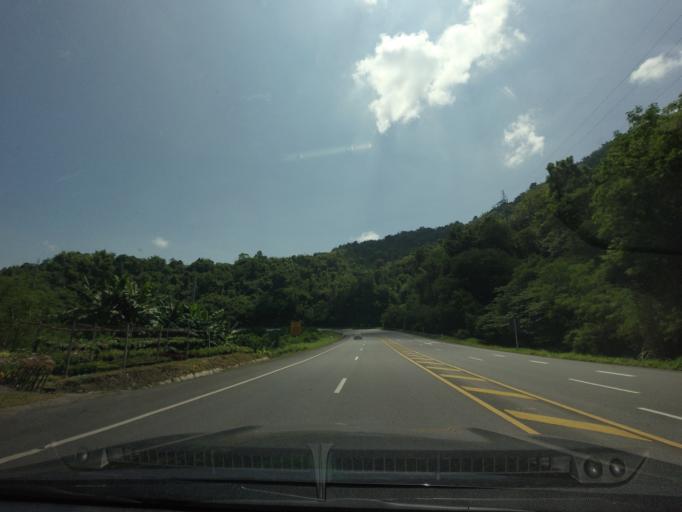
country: TH
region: Phetchabun
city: Khao Kho
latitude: 16.7807
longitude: 101.0922
